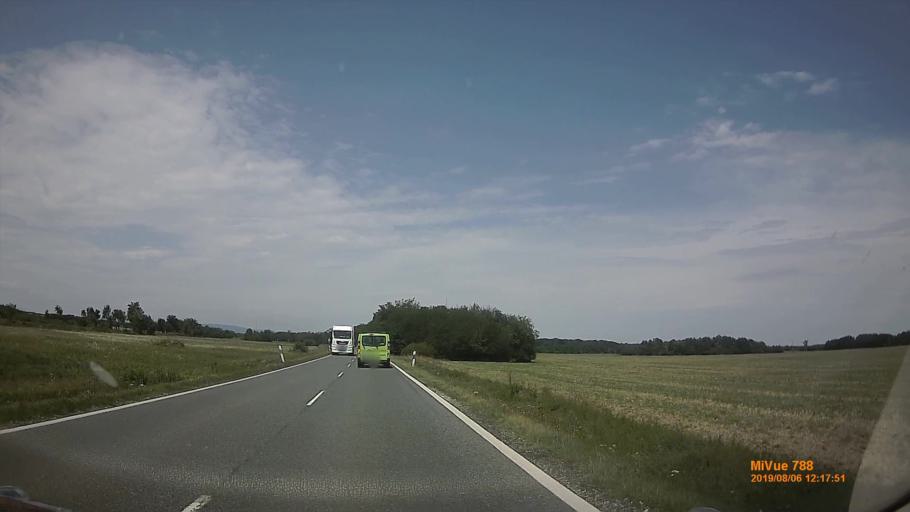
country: HU
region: Vas
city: Vep
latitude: 47.1652
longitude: 16.7842
